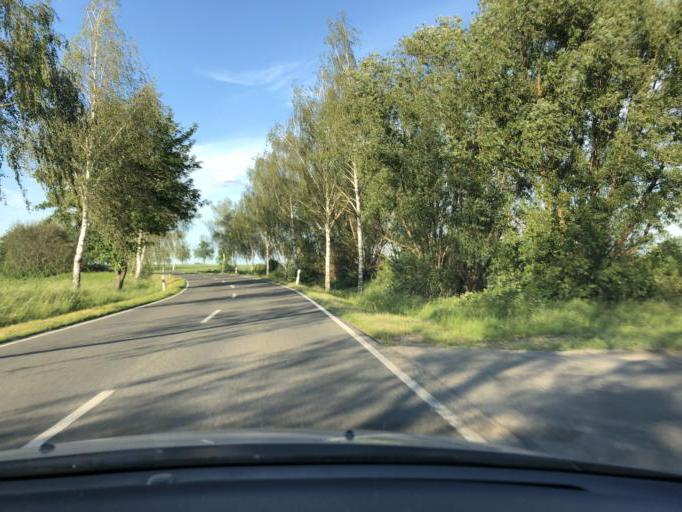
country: DE
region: Saxony
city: Groitzsch
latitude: 51.1333
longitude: 12.2947
